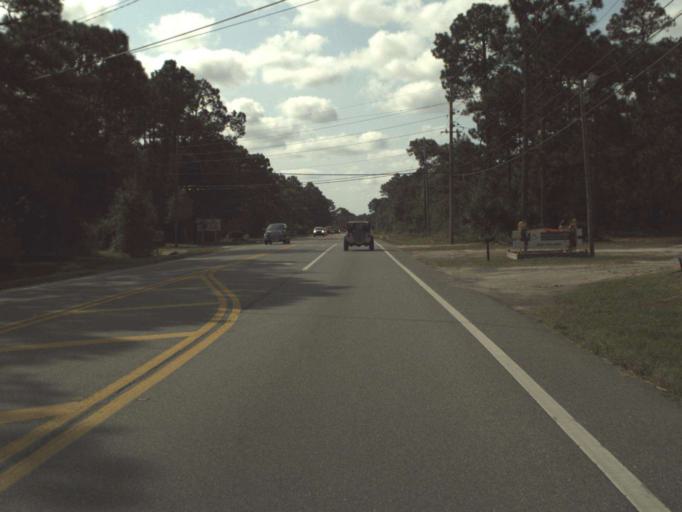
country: US
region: Florida
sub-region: Bay County
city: Pretty Bayou
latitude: 30.2121
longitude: -85.6716
